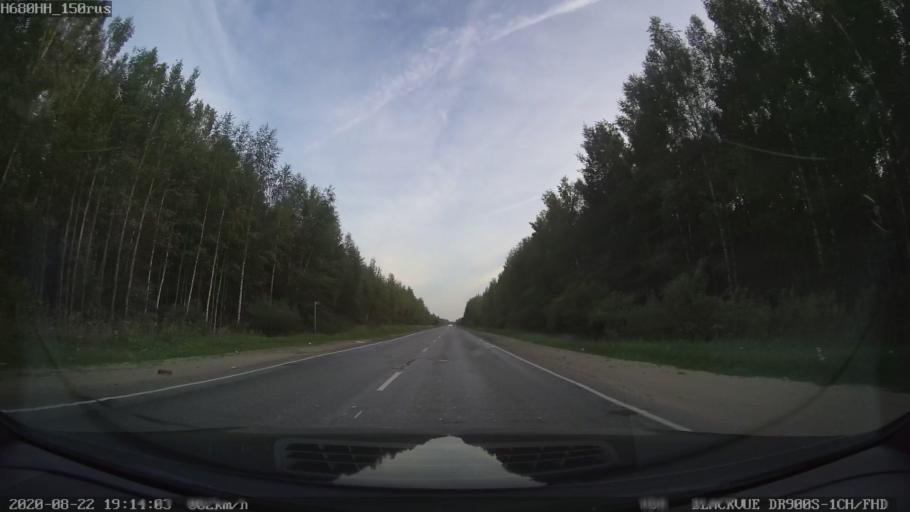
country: RU
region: Tverskaya
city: Sakharovo
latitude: 56.9839
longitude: 36.0237
